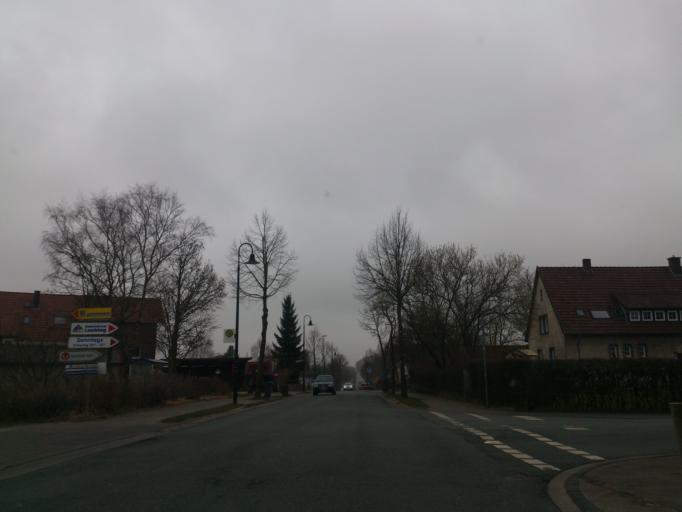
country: DE
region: North Rhine-Westphalia
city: Lichtenau
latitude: 51.6138
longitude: 8.8946
